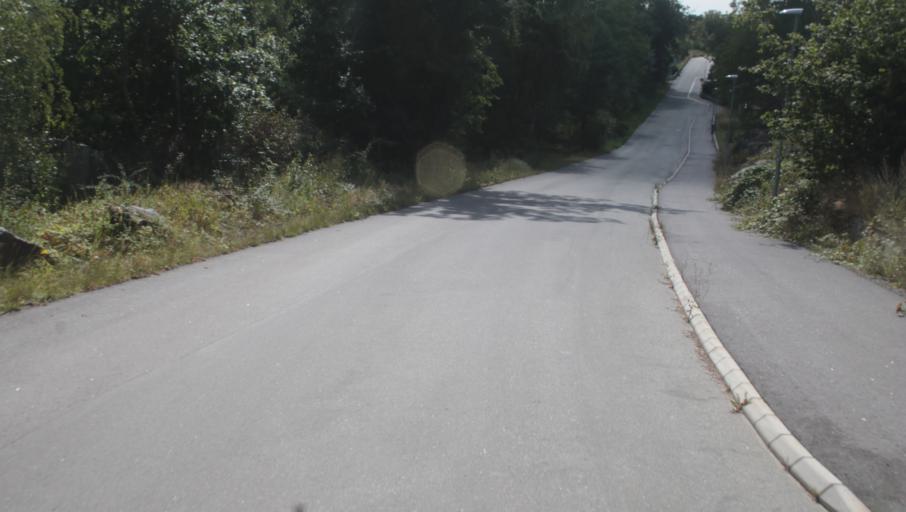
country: SE
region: Blekinge
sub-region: Karlshamns Kommun
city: Karlshamn
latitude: 56.1495
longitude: 14.8504
